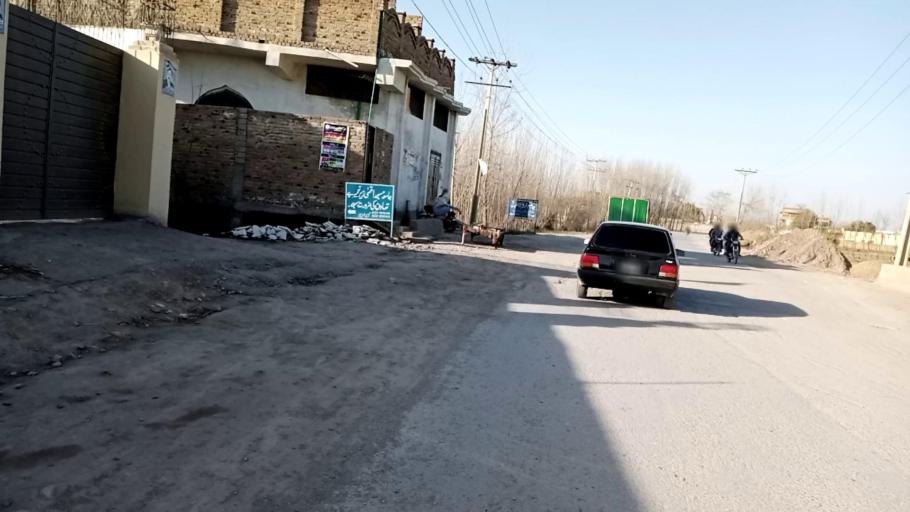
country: PK
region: Khyber Pakhtunkhwa
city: Peshawar
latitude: 34.0662
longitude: 71.5378
